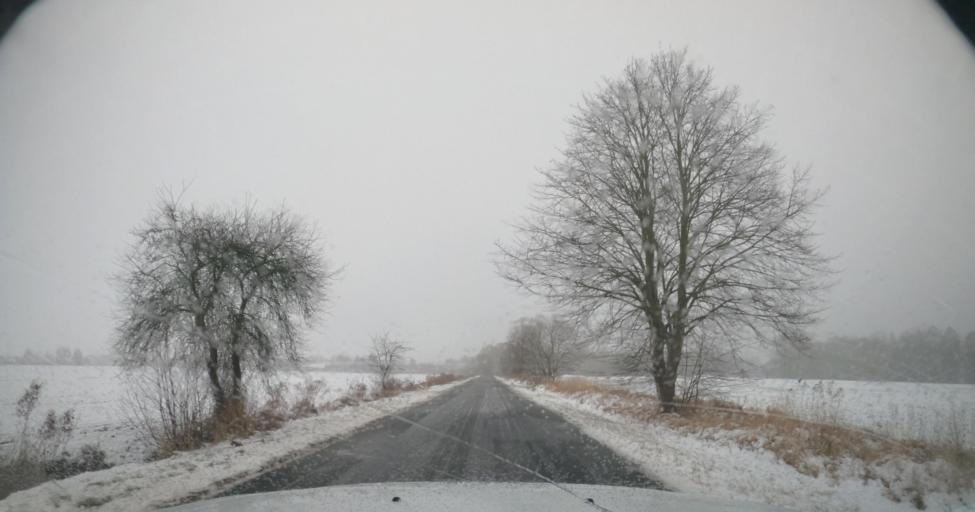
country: PL
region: West Pomeranian Voivodeship
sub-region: Powiat kamienski
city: Golczewo
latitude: 53.7634
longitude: 14.9010
